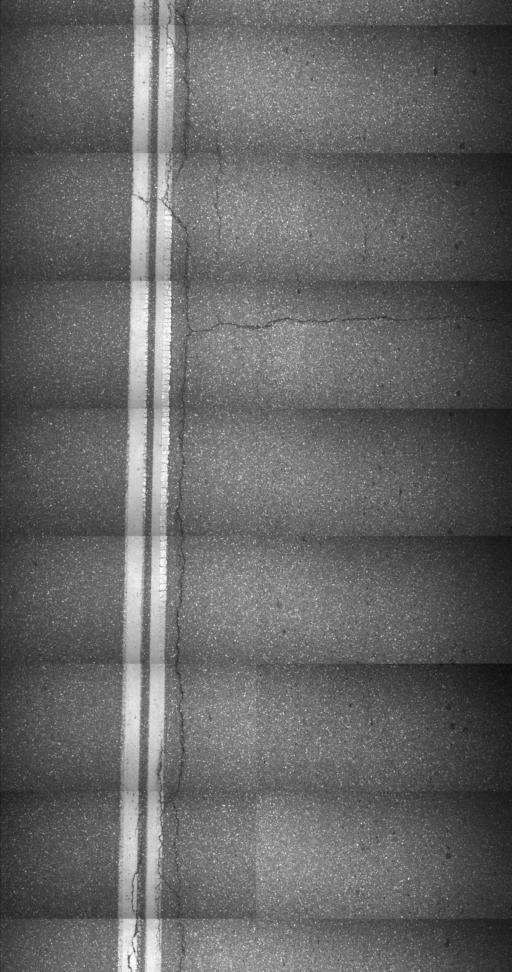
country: US
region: New Hampshire
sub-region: Coos County
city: Stratford
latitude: 44.6265
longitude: -71.5565
